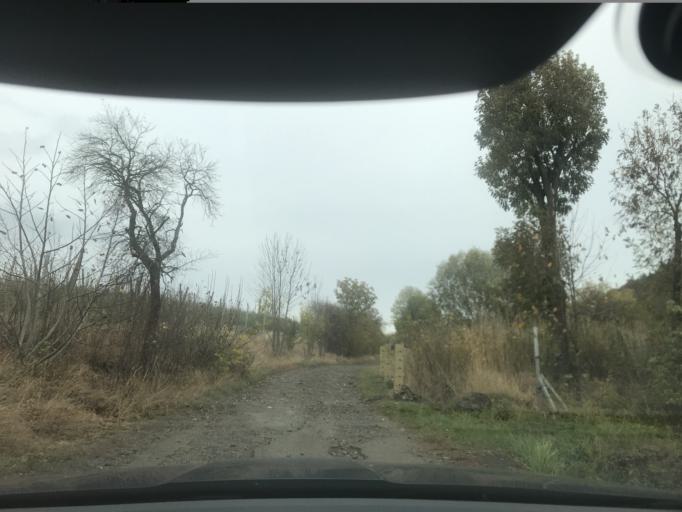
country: CZ
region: Ustecky
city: Trebenice
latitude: 50.4381
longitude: 14.0065
